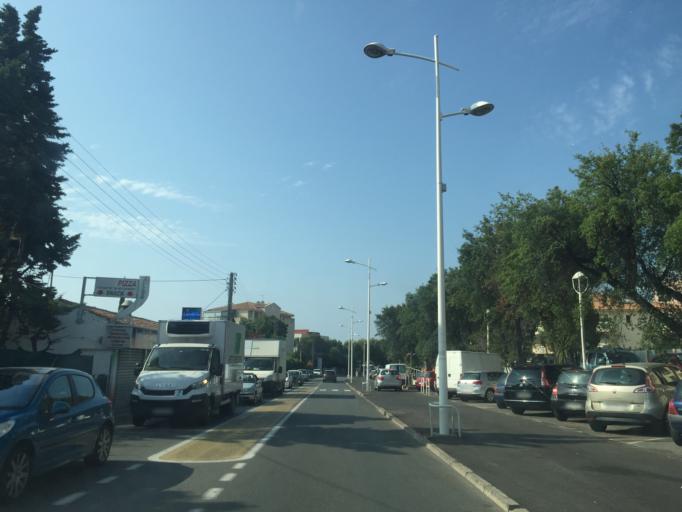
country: FR
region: Provence-Alpes-Cote d'Azur
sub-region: Departement du Var
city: Frejus
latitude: 43.3837
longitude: 6.7223
